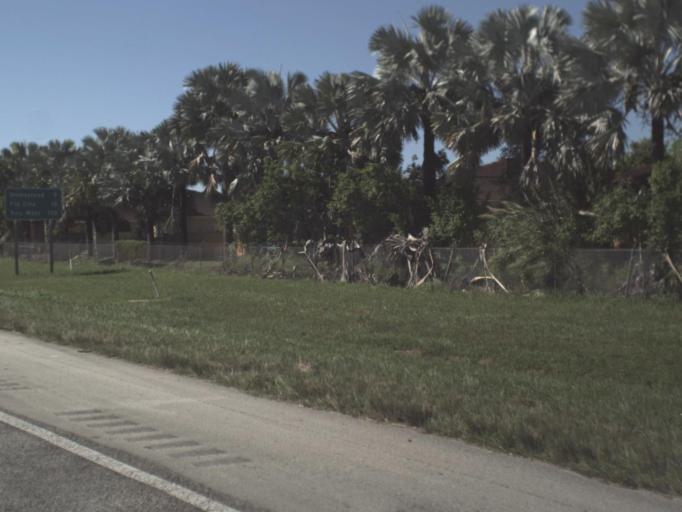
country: US
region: Florida
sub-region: Miami-Dade County
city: Goulds
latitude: 25.5424
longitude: -80.3635
